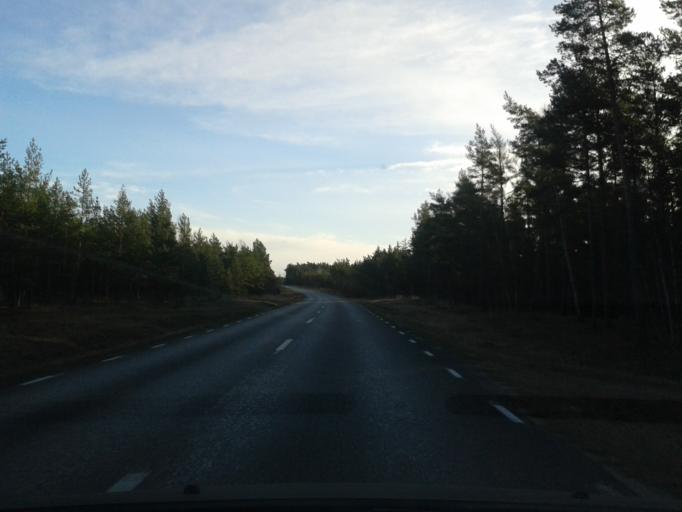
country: SE
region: Gotland
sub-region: Gotland
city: Hemse
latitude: 57.3902
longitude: 18.6488
